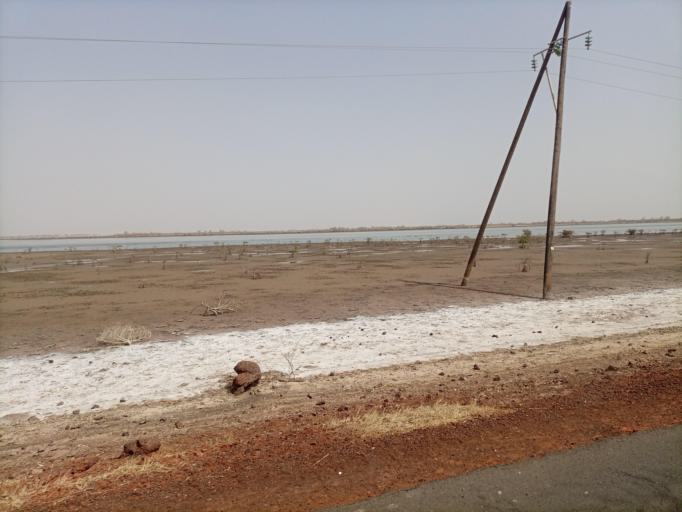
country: SN
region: Fatick
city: Foundiougne
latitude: 14.1916
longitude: -16.4530
